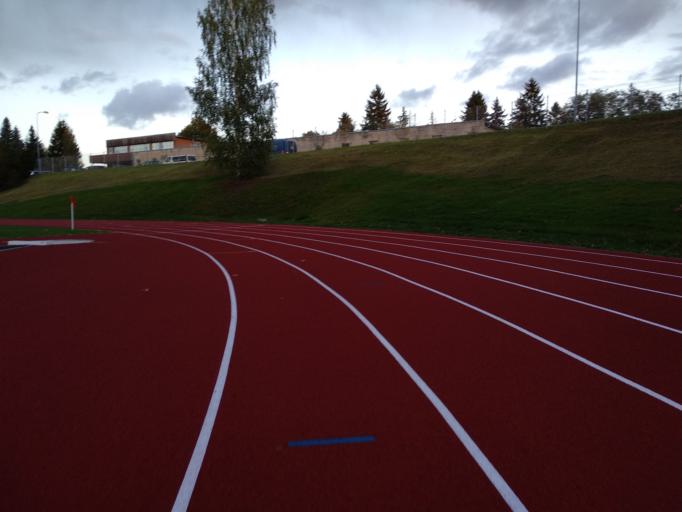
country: EE
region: Polvamaa
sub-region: Polva linn
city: Polva
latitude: 58.0492
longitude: 27.0535
